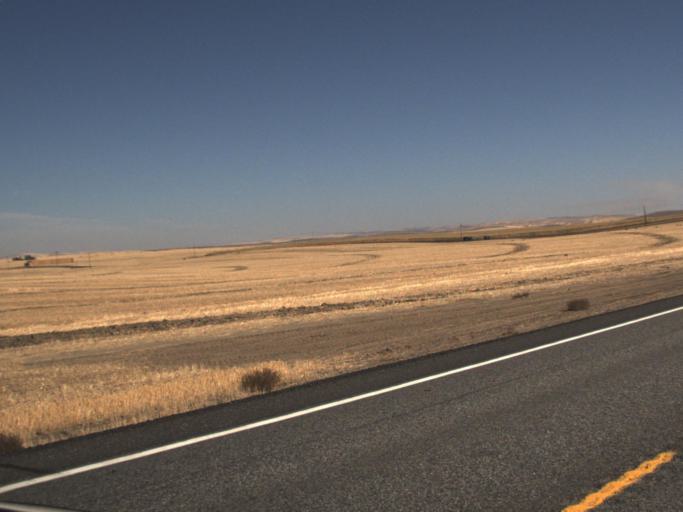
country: US
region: Washington
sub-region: Walla Walla County
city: Garrett
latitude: 46.2963
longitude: -118.6242
